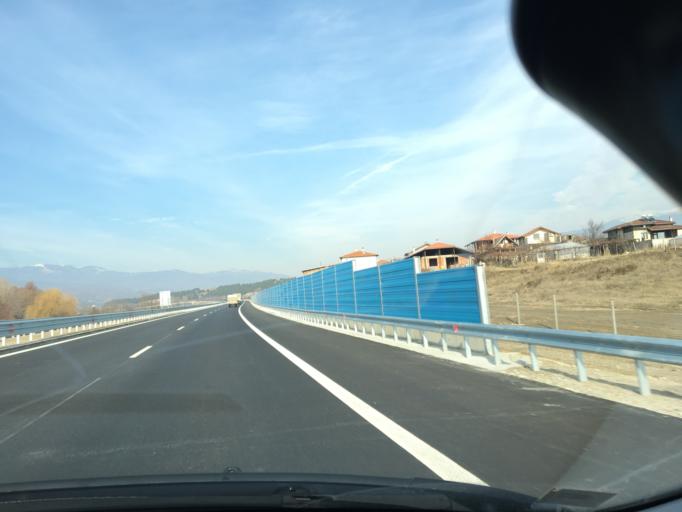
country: BG
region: Blagoevgrad
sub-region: Obshtina Strumyani
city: Strumyani
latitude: 41.6332
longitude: 23.2001
